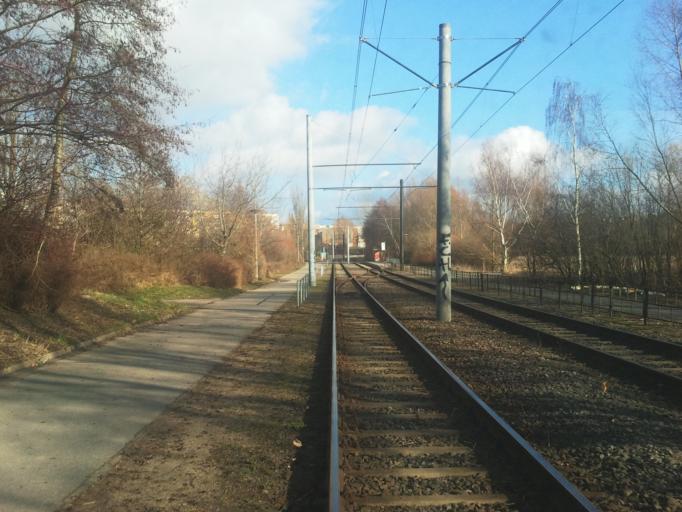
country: DE
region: Mecklenburg-Vorpommern
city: Dierkow-West
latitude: 54.1135
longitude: 12.1433
